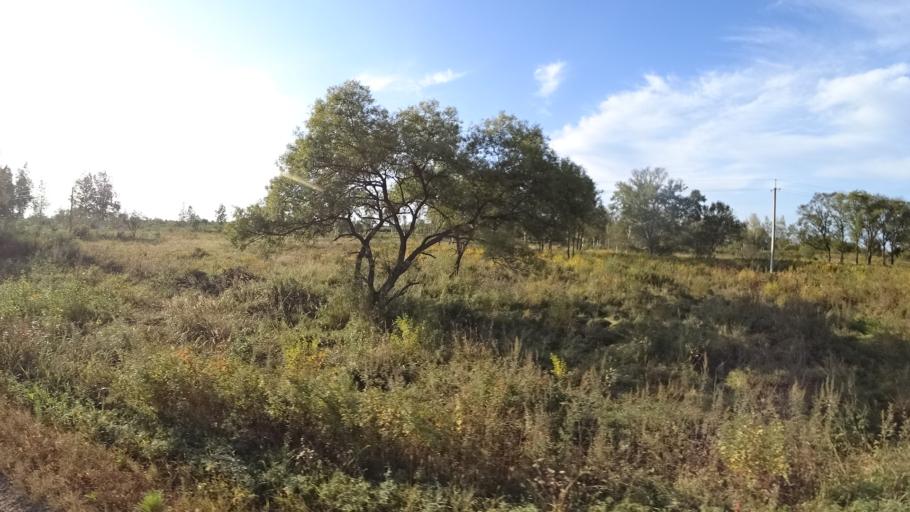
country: RU
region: Amur
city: Arkhara
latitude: 49.3509
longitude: 130.1307
